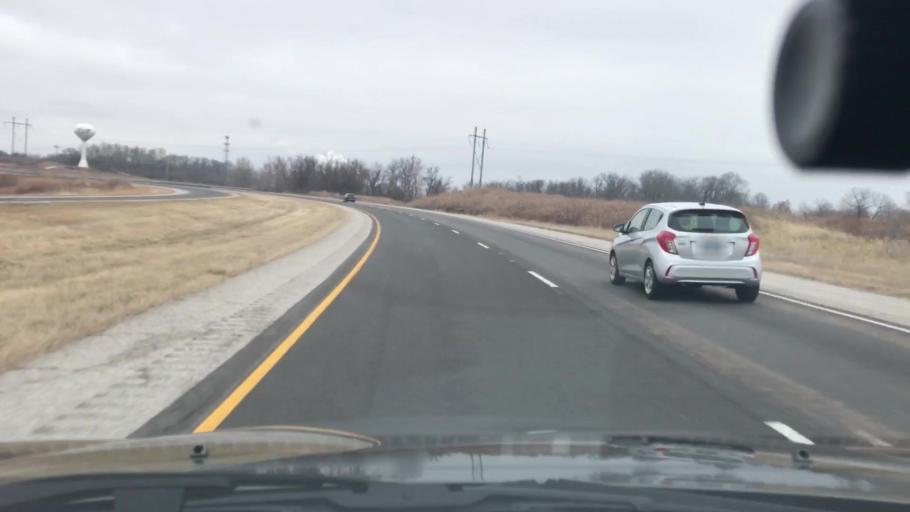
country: US
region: Illinois
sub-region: Madison County
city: Rosewood Heights
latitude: 38.8748
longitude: -90.0614
